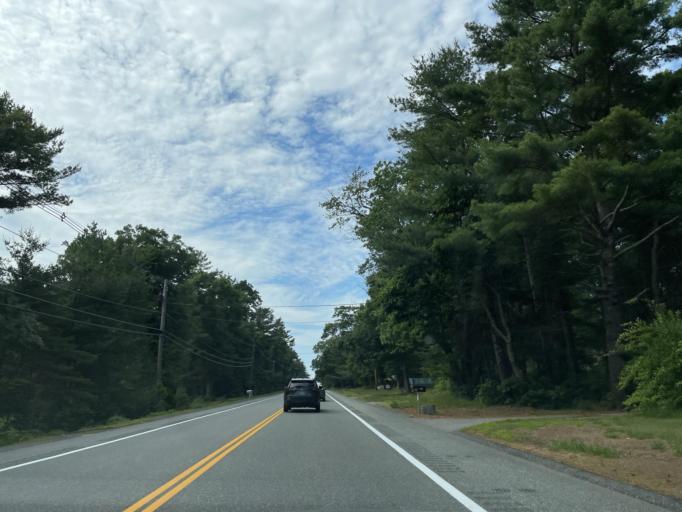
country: US
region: Rhode Island
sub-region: Kent County
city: West Greenwich
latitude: 41.6352
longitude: -71.6861
